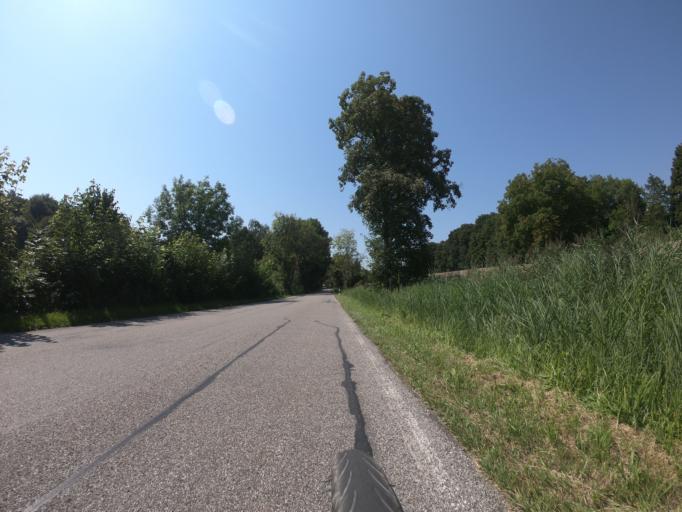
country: DE
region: Bavaria
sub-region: Upper Bavaria
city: Fuerstenfeldbruck
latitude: 48.1700
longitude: 11.2622
